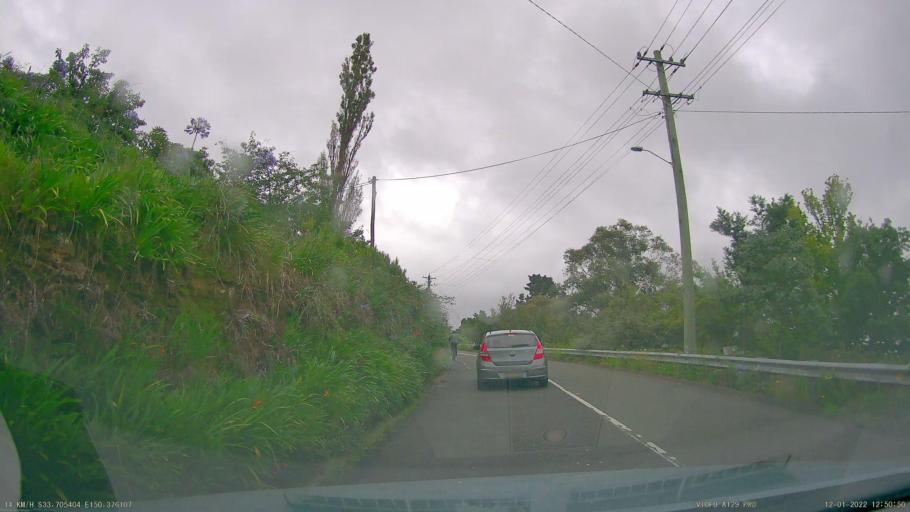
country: AU
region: New South Wales
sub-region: Blue Mountains Municipality
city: Leura
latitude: -33.7053
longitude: 150.3761
